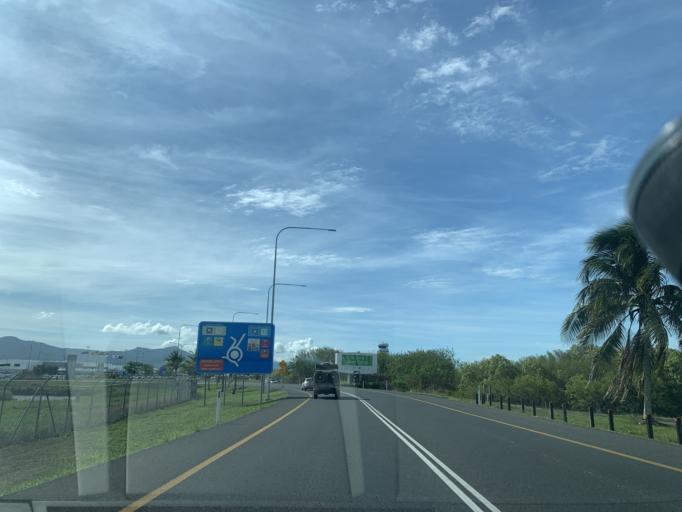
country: AU
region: Queensland
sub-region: Cairns
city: Cairns
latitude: -16.8802
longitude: 145.7590
